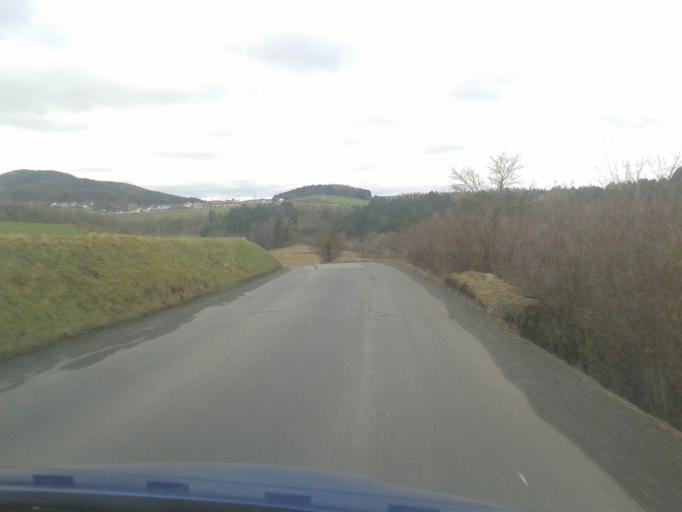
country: CZ
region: Central Bohemia
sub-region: Okres Beroun
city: Kraluv Dvur
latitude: 49.9304
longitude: 14.0570
